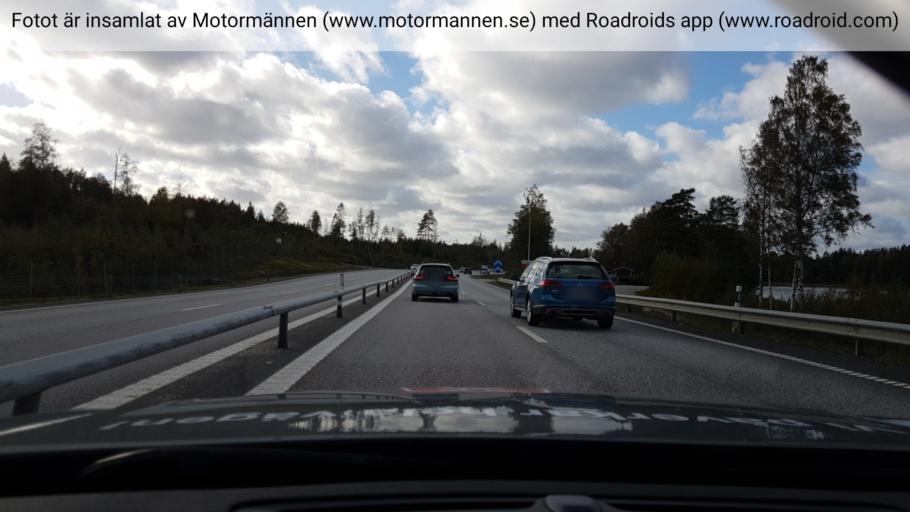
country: SE
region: OErebro
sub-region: Lekebergs Kommun
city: Fjugesta
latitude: 59.2786
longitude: 14.7117
